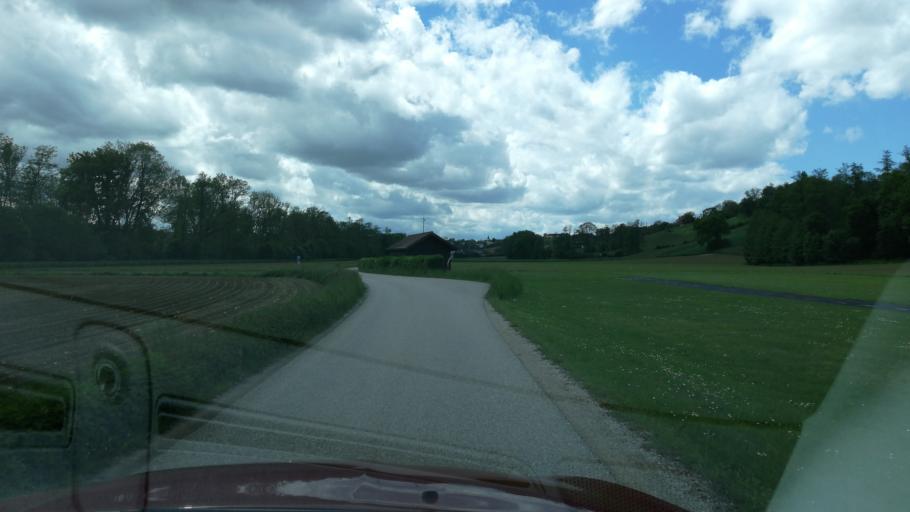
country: AT
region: Upper Austria
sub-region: Politischer Bezirk Linz-Land
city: Traun
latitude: 48.1855
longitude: 14.2212
